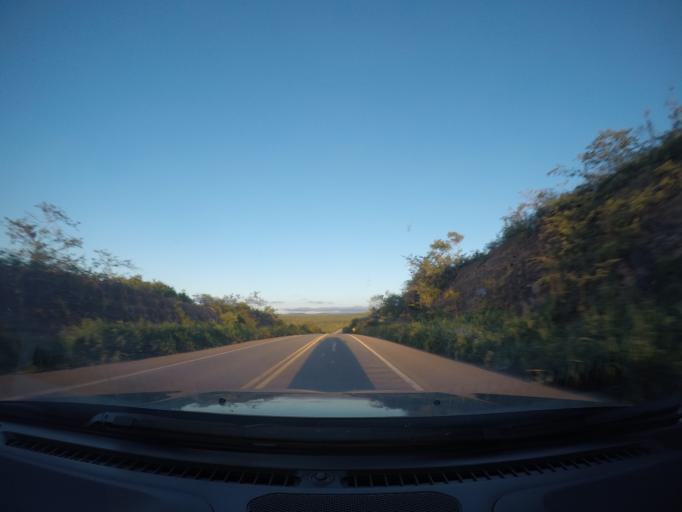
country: BR
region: Bahia
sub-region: Seabra
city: Seabra
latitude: -12.3951
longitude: -41.9300
